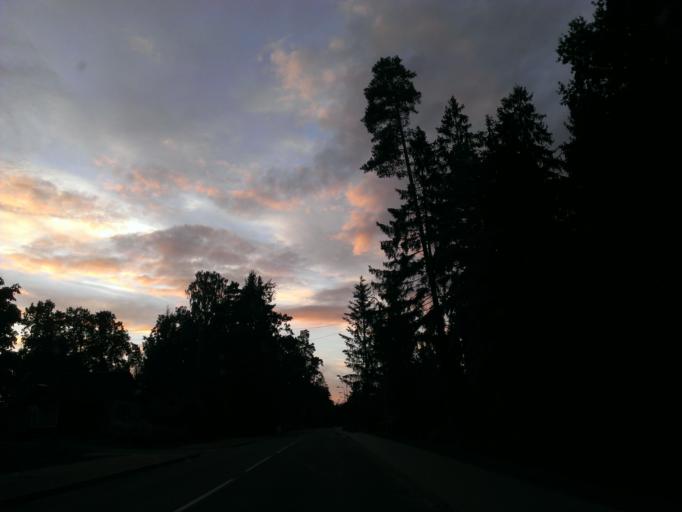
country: LV
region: Ogre
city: Ogre
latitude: 56.8218
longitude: 24.6104
